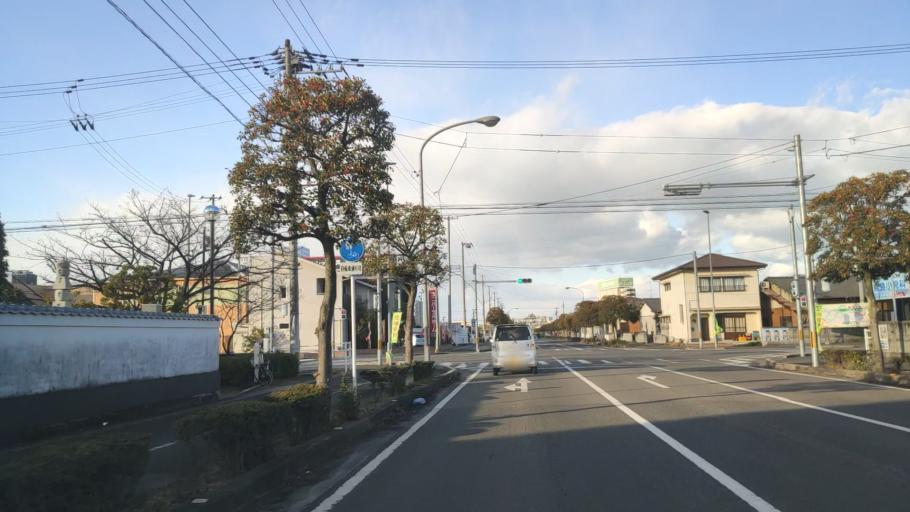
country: JP
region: Ehime
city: Saijo
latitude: 33.9237
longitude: 133.1840
